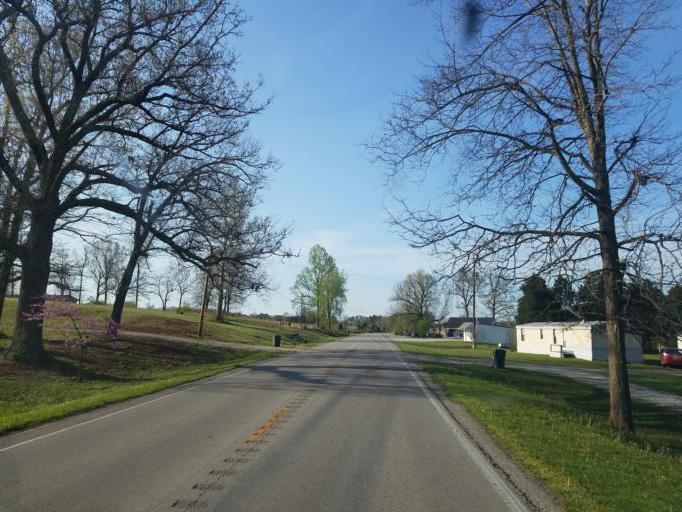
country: US
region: Kentucky
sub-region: Hart County
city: Munfordville
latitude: 37.4433
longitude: -85.8914
